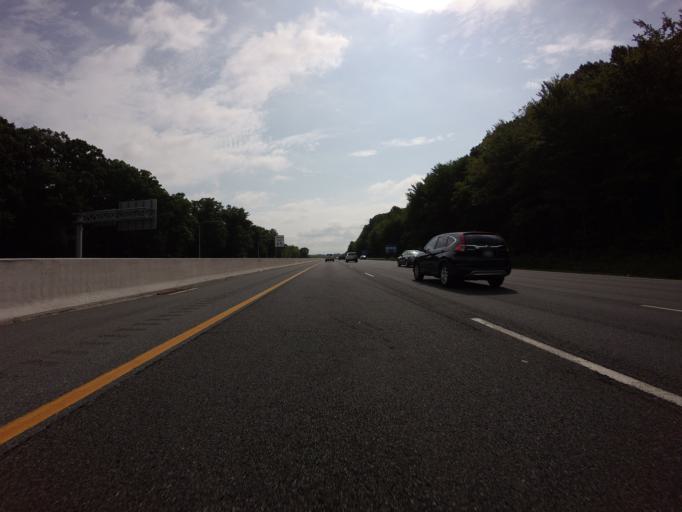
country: US
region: Delaware
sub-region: New Castle County
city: Brookside
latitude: 39.6468
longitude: -75.7562
